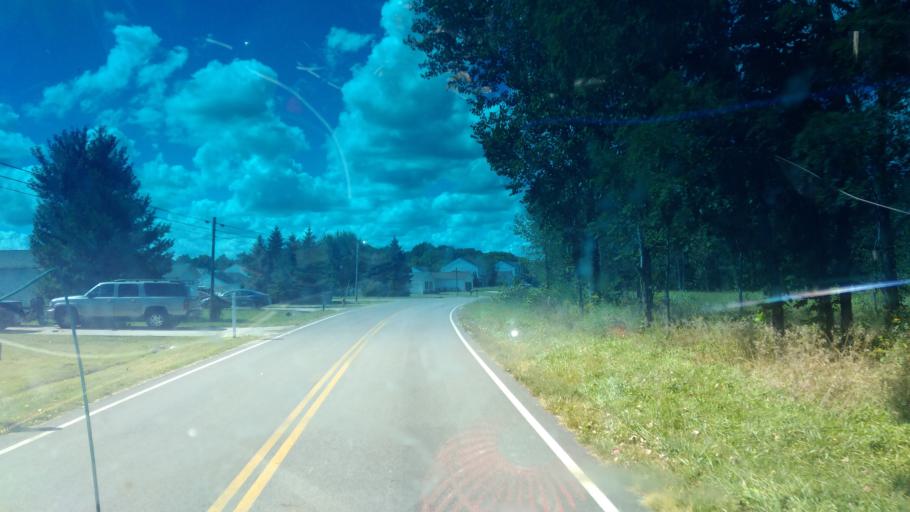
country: US
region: Ohio
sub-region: Union County
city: Marysville
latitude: 40.1811
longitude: -83.4451
